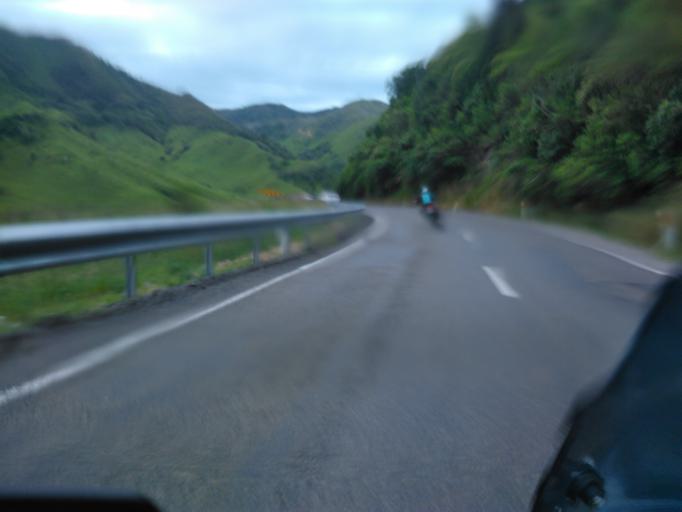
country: NZ
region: Bay of Plenty
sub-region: Opotiki District
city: Opotiki
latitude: -38.3602
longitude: 177.4560
